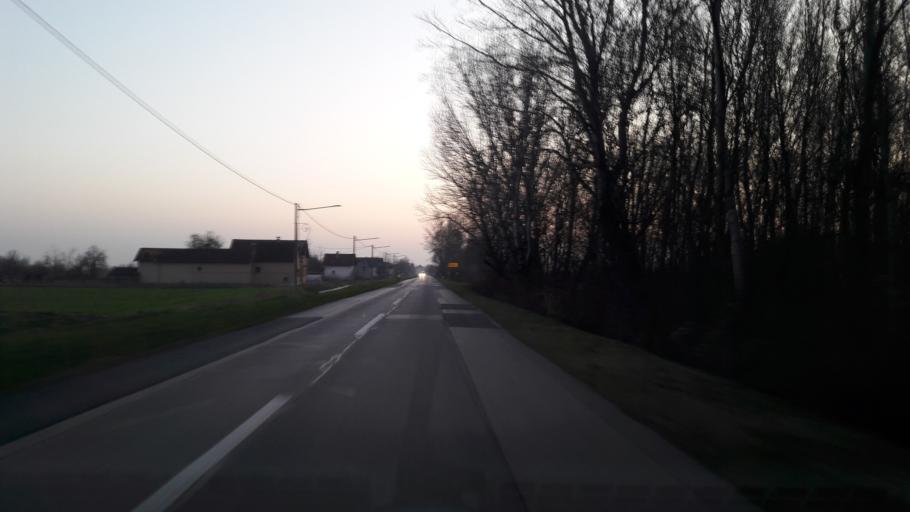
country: HR
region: Vukovarsko-Srijemska
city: Nijemci
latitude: 45.1911
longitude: 19.0179
